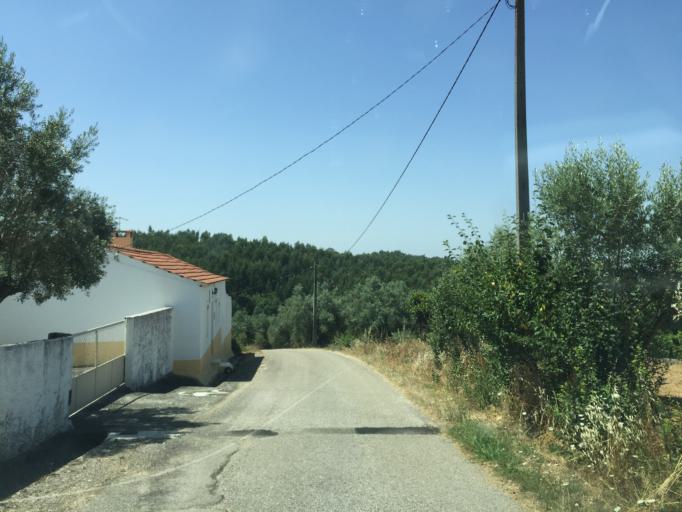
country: PT
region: Santarem
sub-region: Ferreira do Zezere
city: Ferreira do Zezere
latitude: 39.6544
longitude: -8.3022
